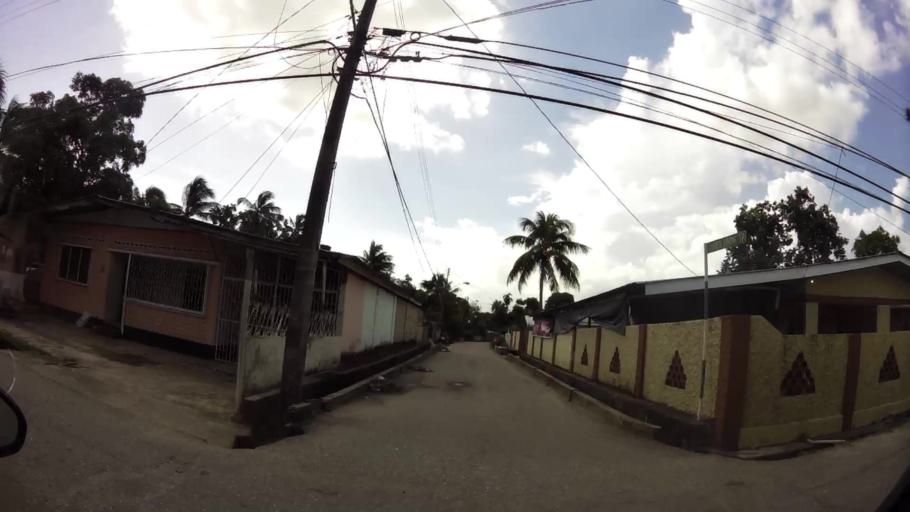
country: TT
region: Tunapuna/Piarco
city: Arouca
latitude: 10.6161
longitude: -61.3255
